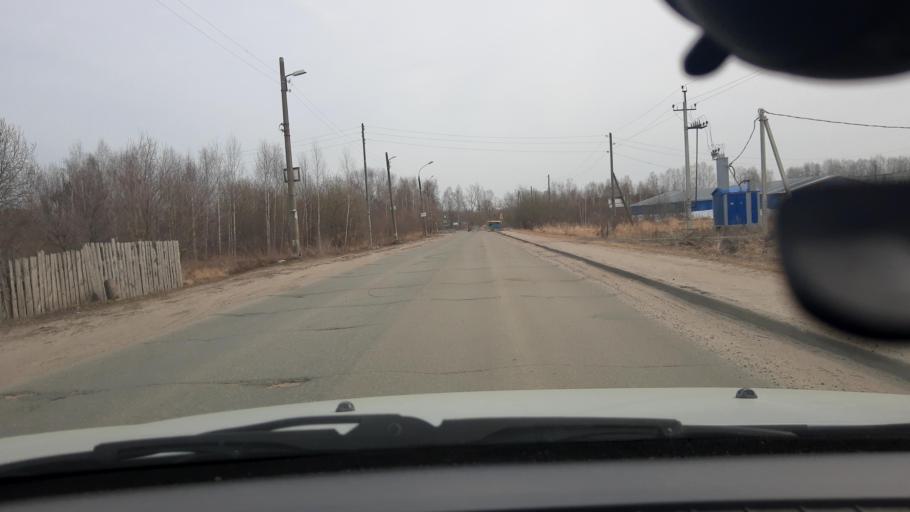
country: RU
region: Nizjnij Novgorod
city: Gidrotorf
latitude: 56.4658
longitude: 43.5457
